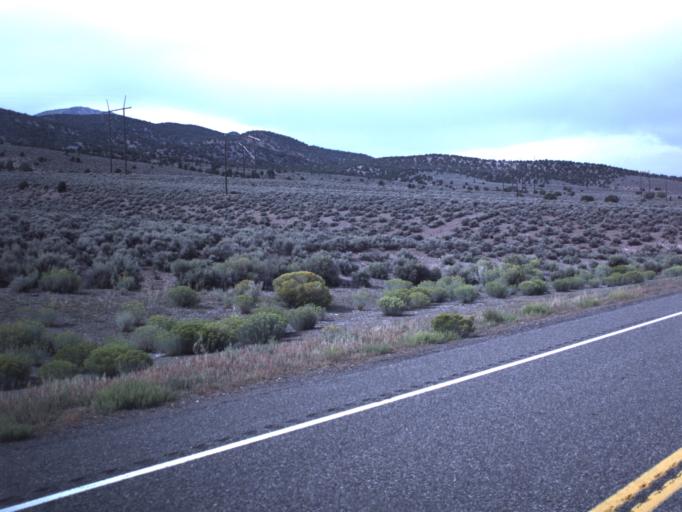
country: US
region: Utah
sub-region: Piute County
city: Junction
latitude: 38.3191
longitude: -112.2204
